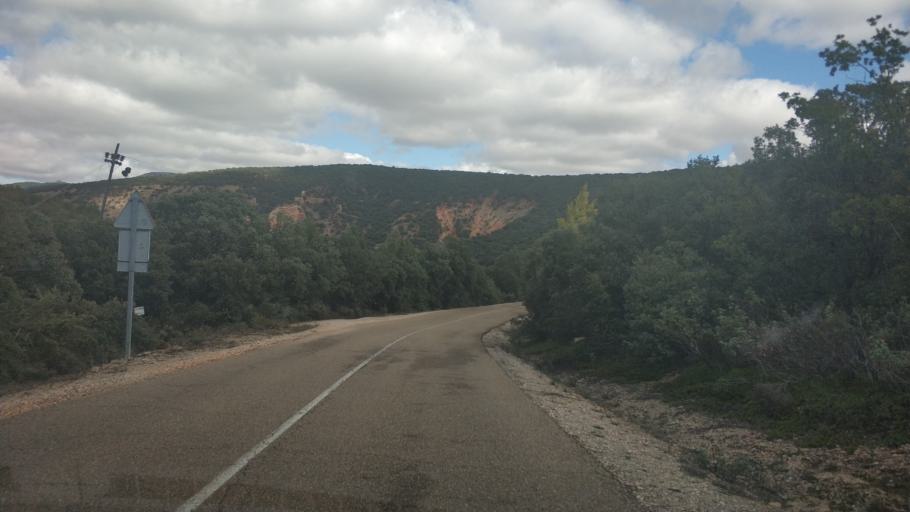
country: ES
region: Castille and Leon
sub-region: Provincia de Burgos
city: Retuerta
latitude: 42.0442
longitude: -3.4938
